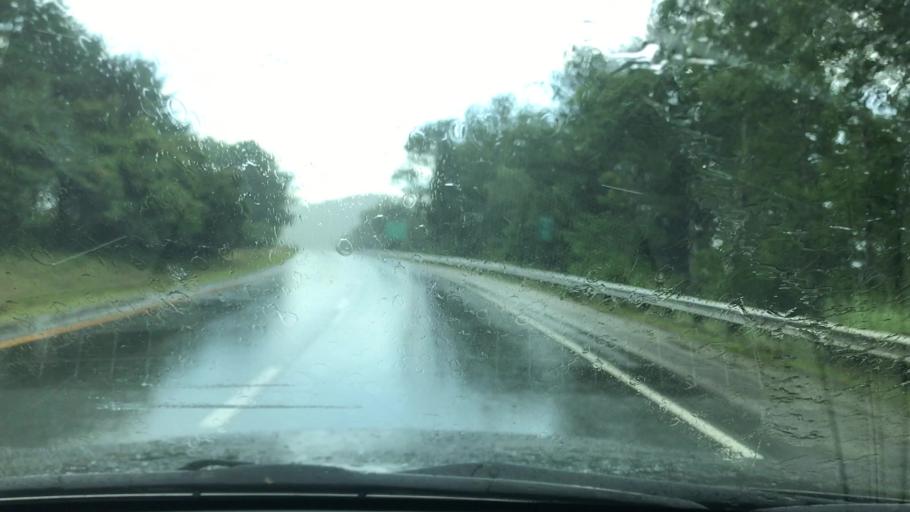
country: US
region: New Hampshire
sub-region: Grafton County
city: Littleton
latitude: 44.2940
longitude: -71.7565
